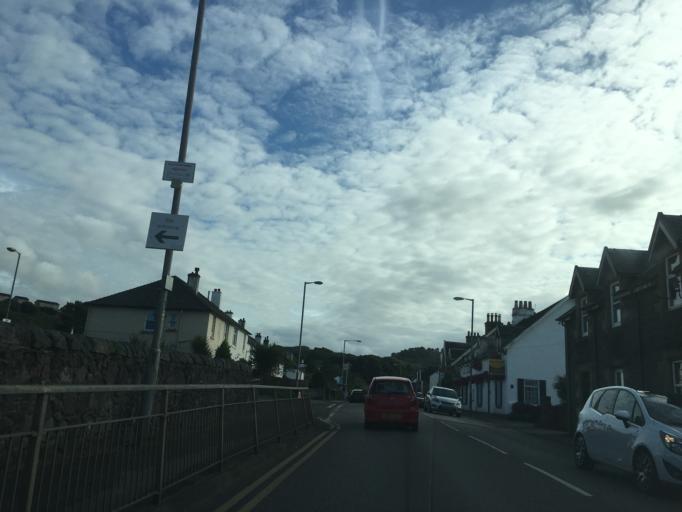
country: GB
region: Scotland
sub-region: Argyll and Bute
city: Oban
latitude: 56.4067
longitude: -5.4694
